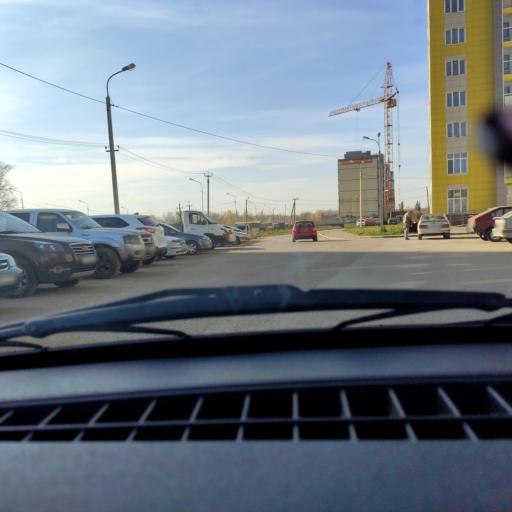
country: RU
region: Bashkortostan
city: Ufa
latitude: 54.6843
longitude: 55.9840
